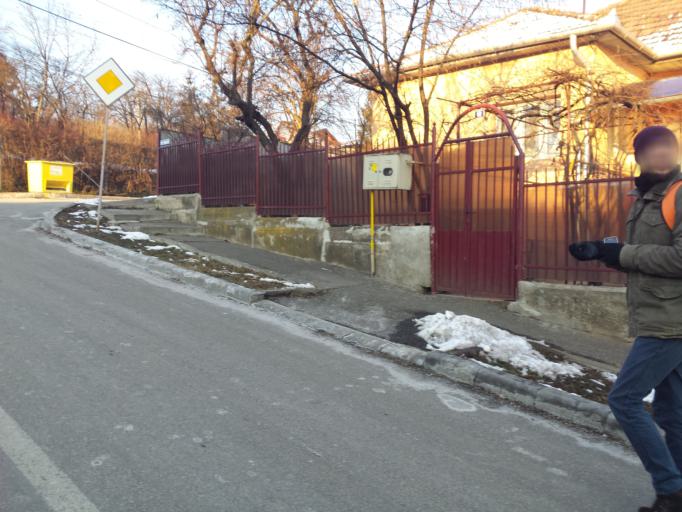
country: RO
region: Cluj
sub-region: Municipiul Cluj-Napoca
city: Cluj-Napoca
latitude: 46.7918
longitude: 23.5862
